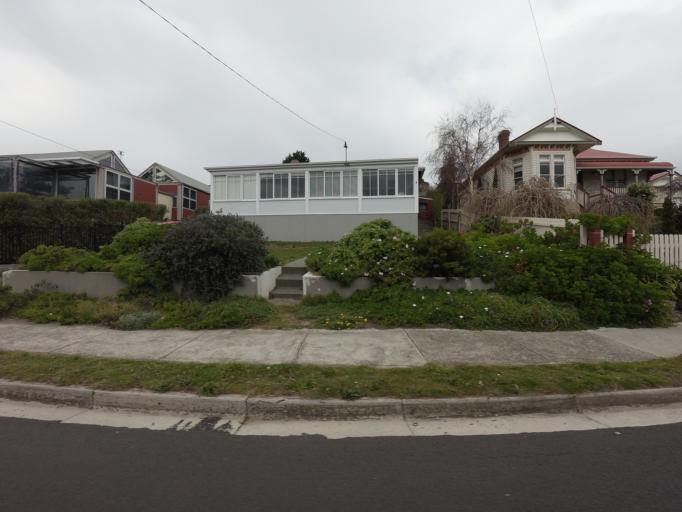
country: AU
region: Tasmania
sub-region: Clarence
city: Bellerive
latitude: -42.8750
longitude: 147.3644
